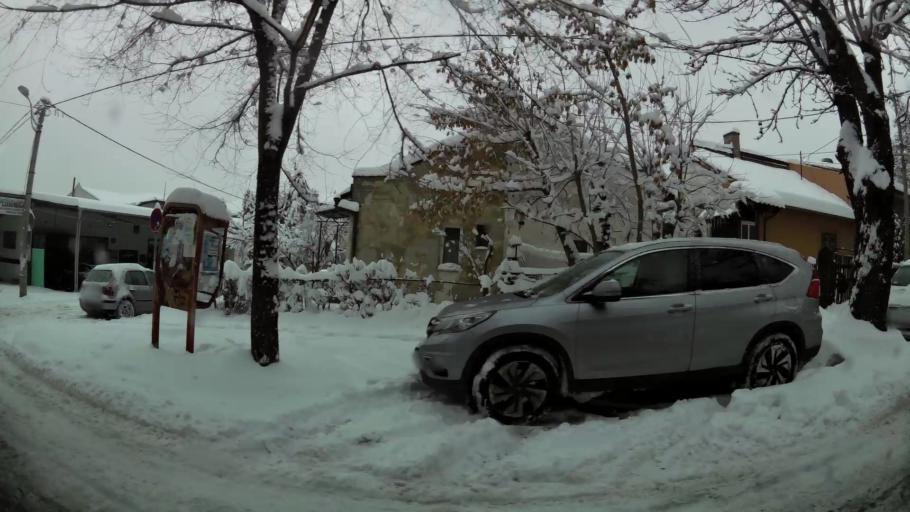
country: RS
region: Central Serbia
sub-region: Belgrade
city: Vracar
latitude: 44.7884
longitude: 20.4885
